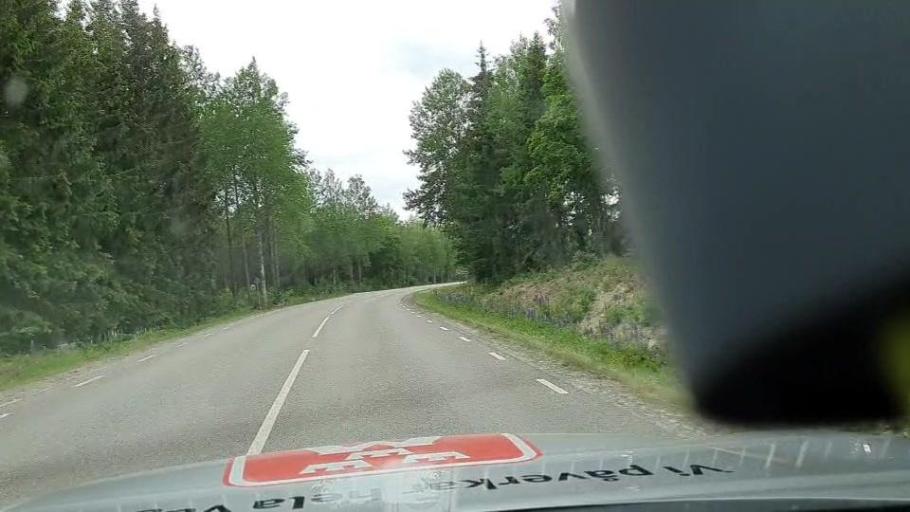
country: SE
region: Kalmar
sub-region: Emmaboda Kommun
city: Emmaboda
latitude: 56.5305
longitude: 15.5416
